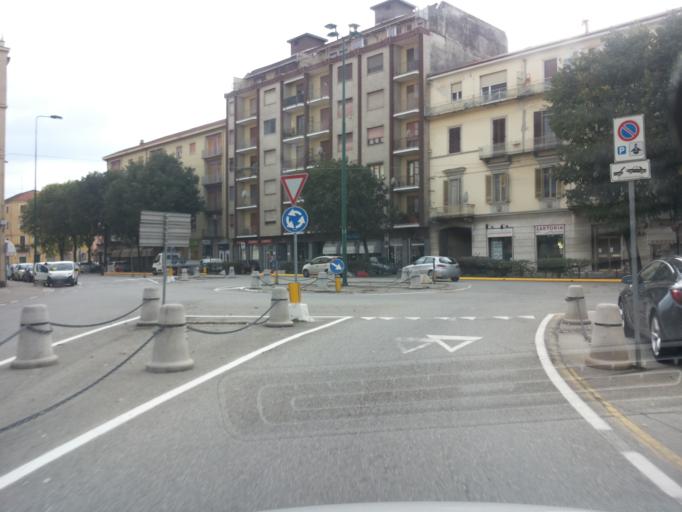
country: IT
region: Piedmont
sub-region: Provincia di Alessandria
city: Casale Monferrato
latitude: 45.1302
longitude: 8.4509
